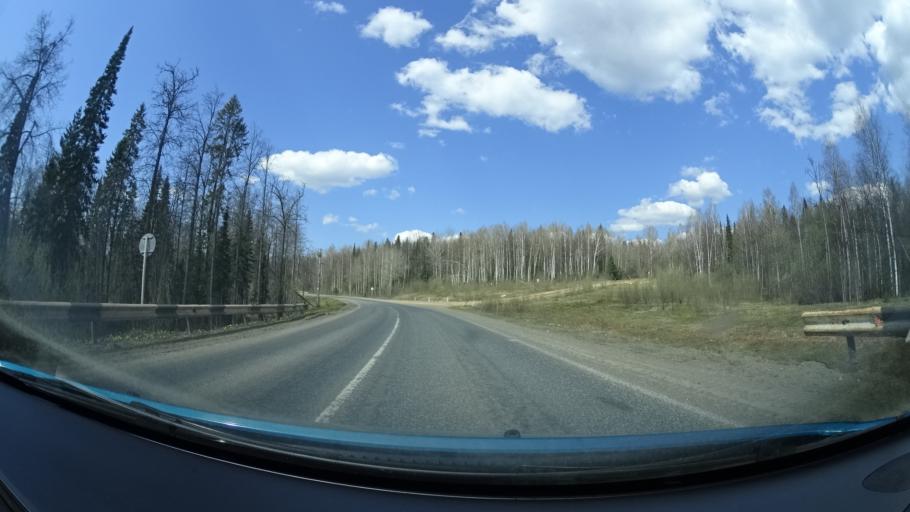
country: RU
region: Perm
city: Yugo-Kamskiy
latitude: 57.6046
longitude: 55.6559
